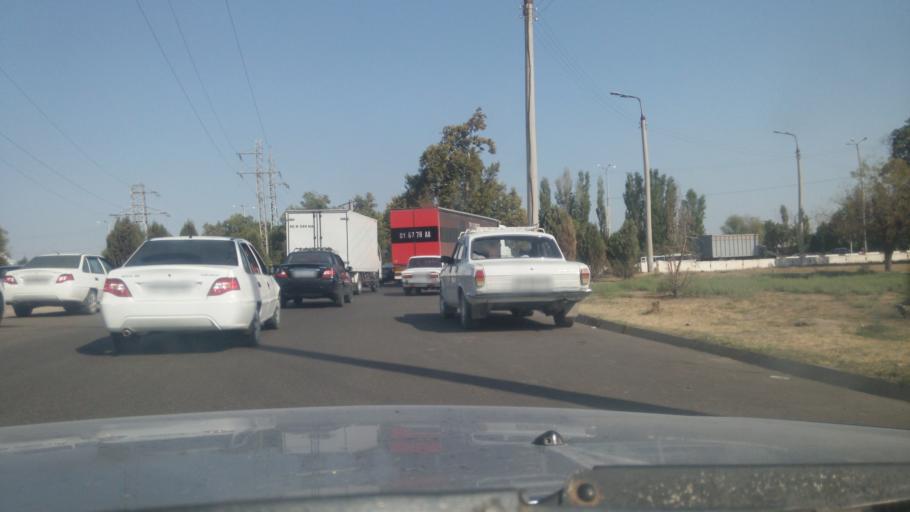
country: UZ
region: Toshkent Shahri
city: Tashkent
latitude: 41.2411
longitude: 69.1682
